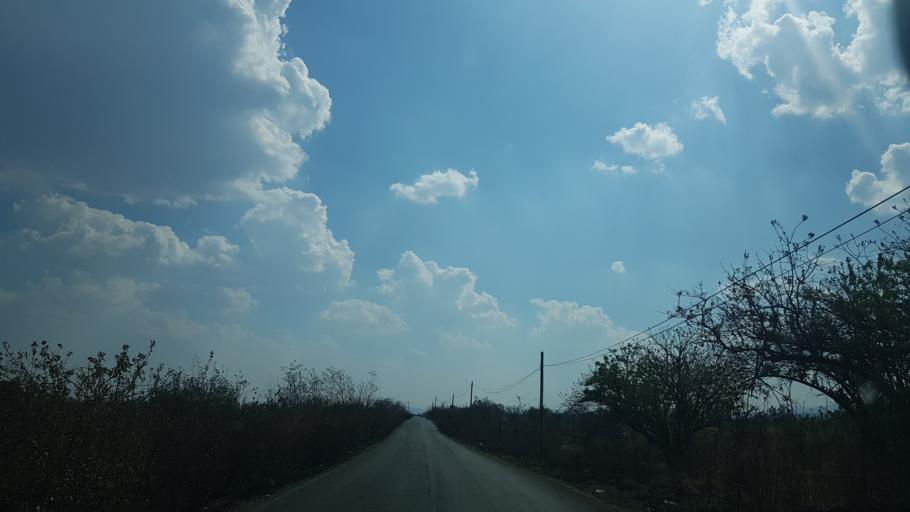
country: MX
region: Puebla
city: Atlixco
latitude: 18.9073
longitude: -98.4789
